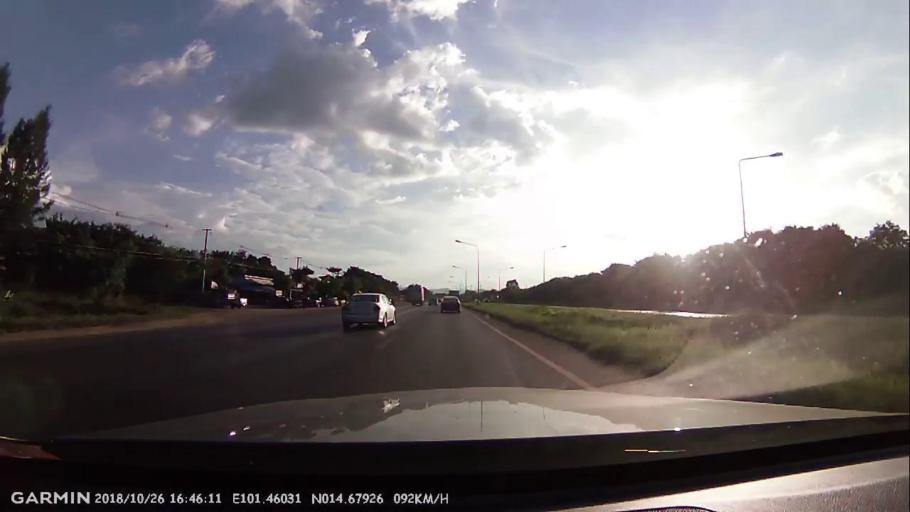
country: TH
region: Nakhon Ratchasima
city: Pak Chong
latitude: 14.6773
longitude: 101.4592
